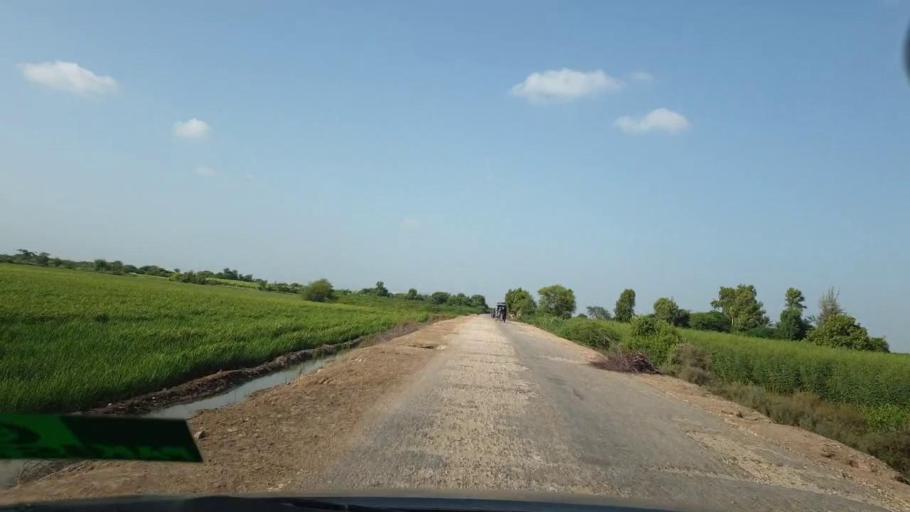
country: PK
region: Sindh
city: Tando Bago
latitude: 24.7087
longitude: 69.1923
